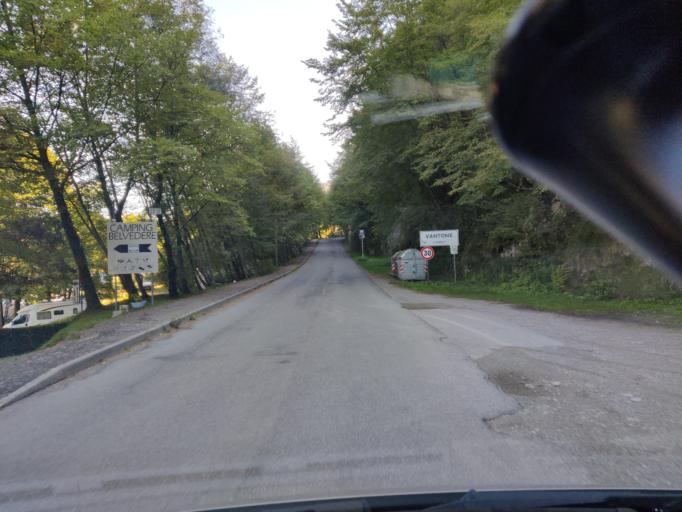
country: IT
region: Lombardy
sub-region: Provincia di Brescia
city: Anfo
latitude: 45.7523
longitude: 10.4940
